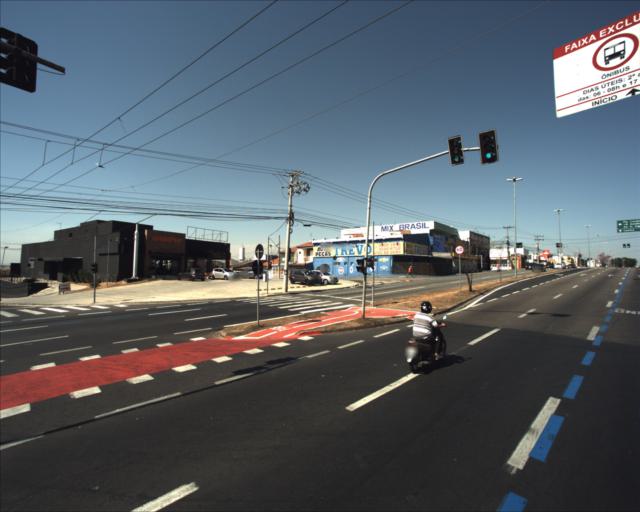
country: BR
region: Sao Paulo
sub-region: Sorocaba
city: Sorocaba
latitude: -23.4576
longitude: -47.4804
